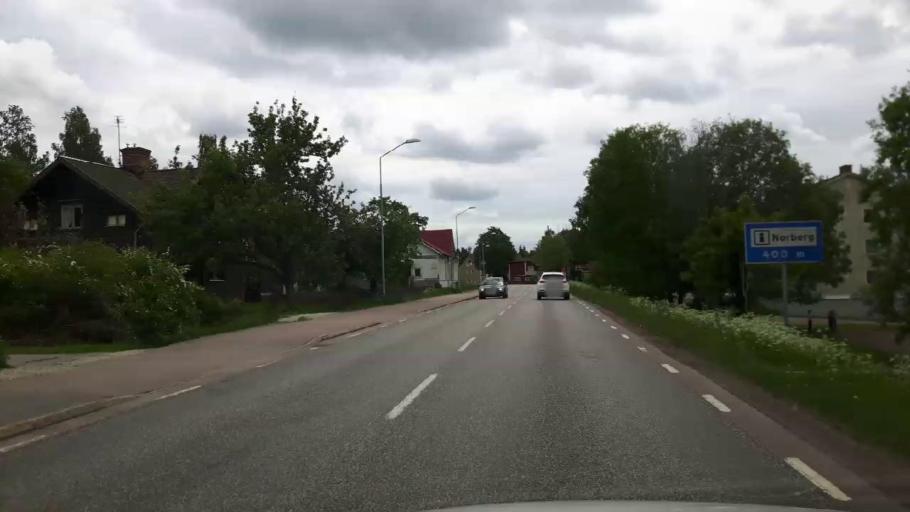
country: SE
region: Vaestmanland
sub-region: Norbergs Kommun
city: Norberg
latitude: 60.0955
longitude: 15.9321
